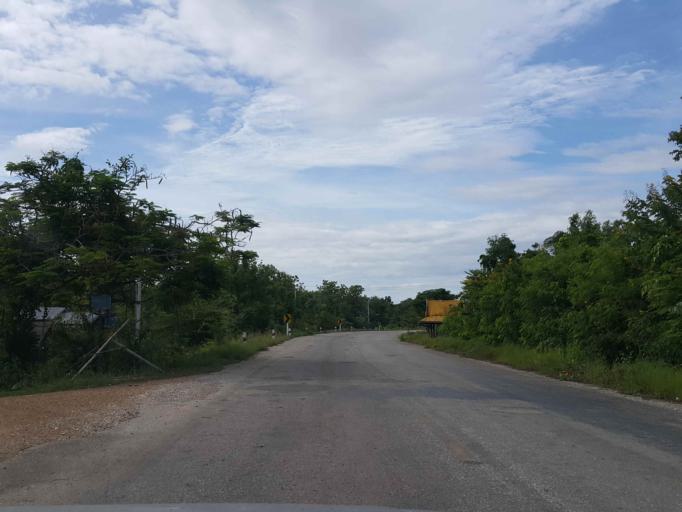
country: TH
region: Sukhothai
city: Thung Saliam
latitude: 17.3031
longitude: 99.5270
